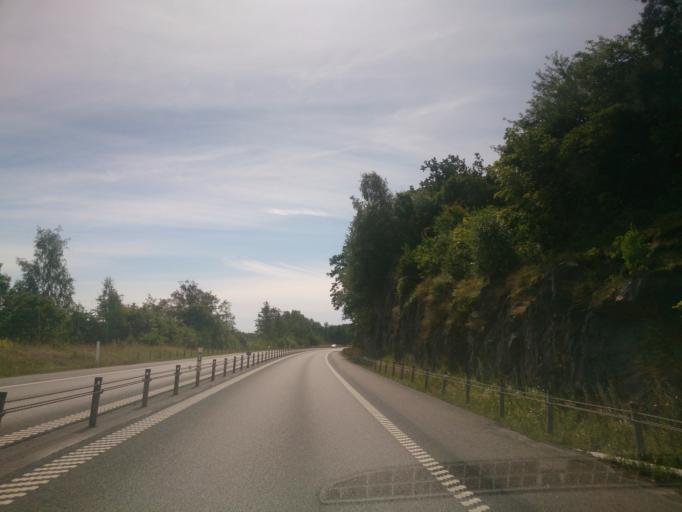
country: SE
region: OEstergoetland
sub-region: Valdemarsviks Kommun
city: Gusum
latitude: 58.3273
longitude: 16.4732
